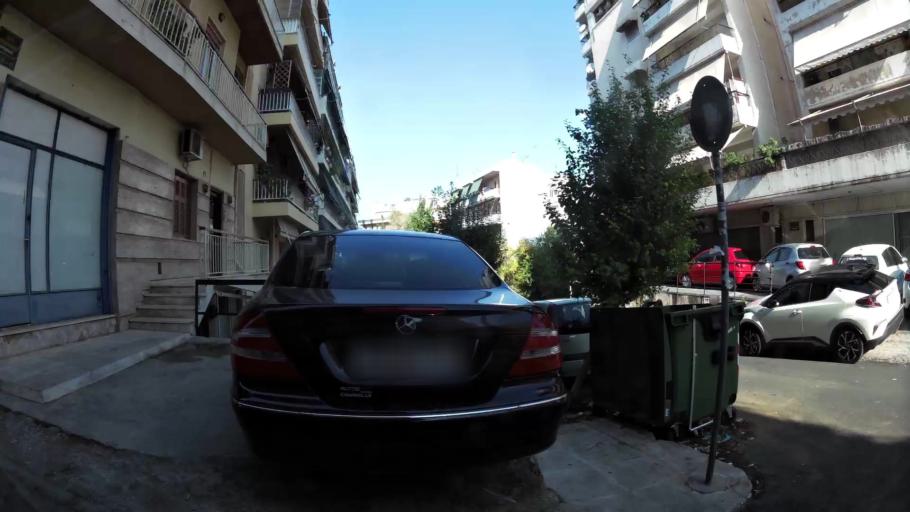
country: GR
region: Attica
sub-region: Nomarchia Athinas
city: Kaisariani
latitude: 37.9809
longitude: 23.7697
